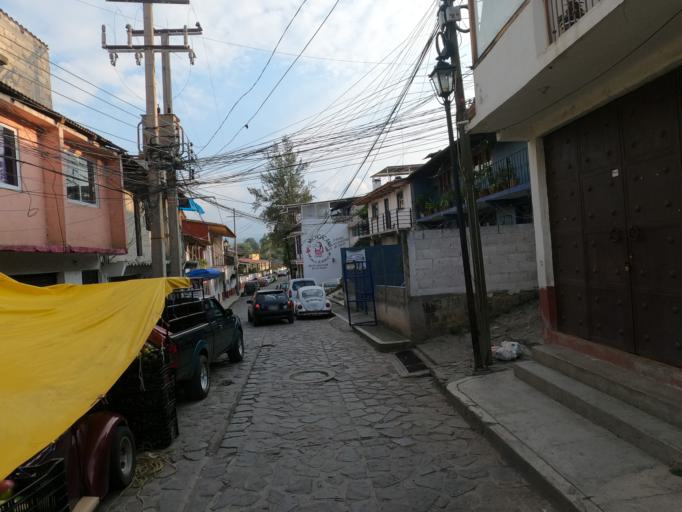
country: MX
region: Mexico
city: Valle de Bravo
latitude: 19.2013
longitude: -100.1290
